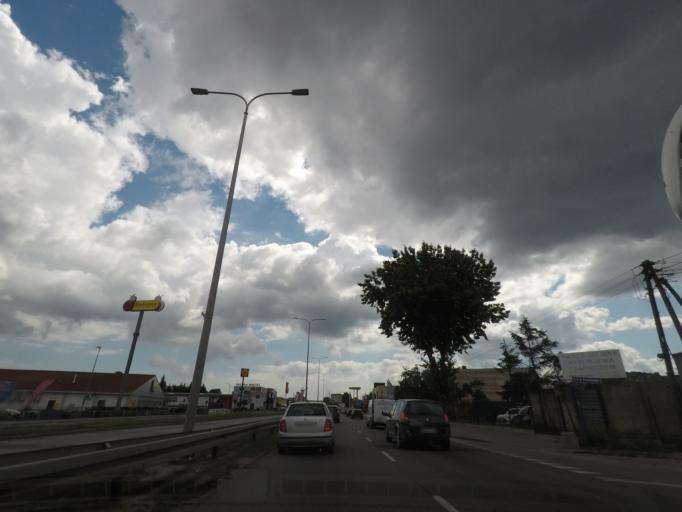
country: PL
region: Pomeranian Voivodeship
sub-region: Powiat wejherowski
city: Rumia
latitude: 54.5742
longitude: 18.3816
